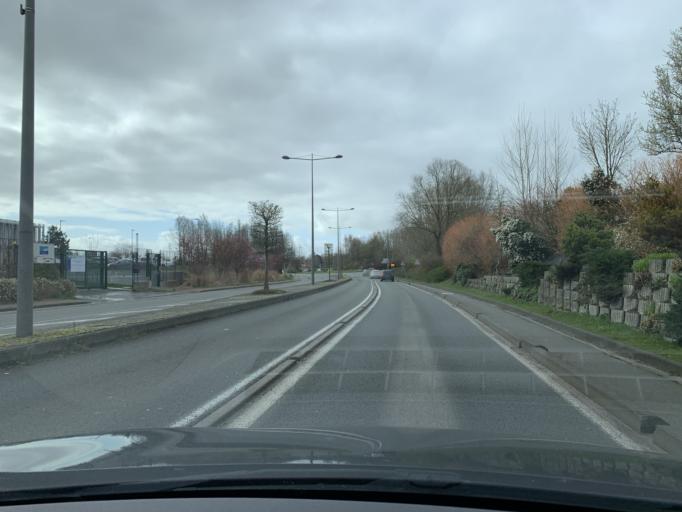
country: FR
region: Nord-Pas-de-Calais
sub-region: Departement du Nord
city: Waziers
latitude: 50.3852
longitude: 3.0981
